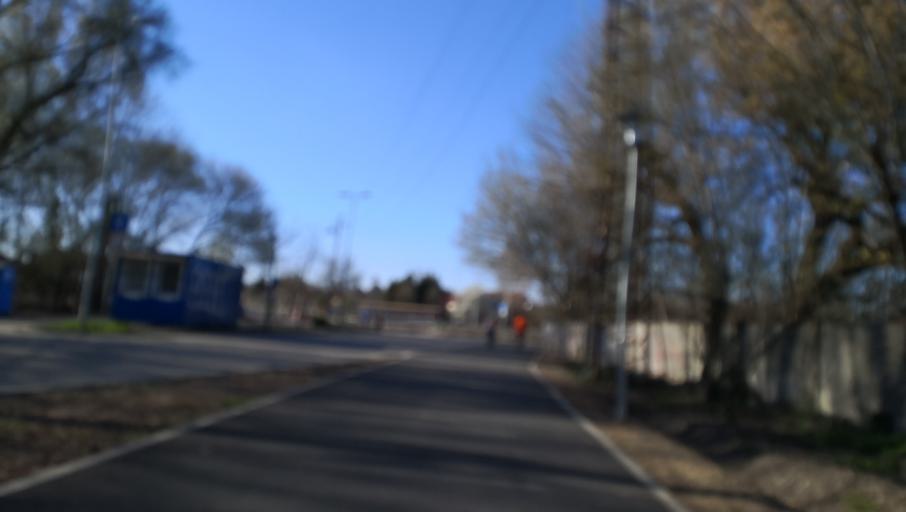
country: HU
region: Budapest
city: Budapest XVII. keruelet
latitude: 47.4908
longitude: 19.2830
